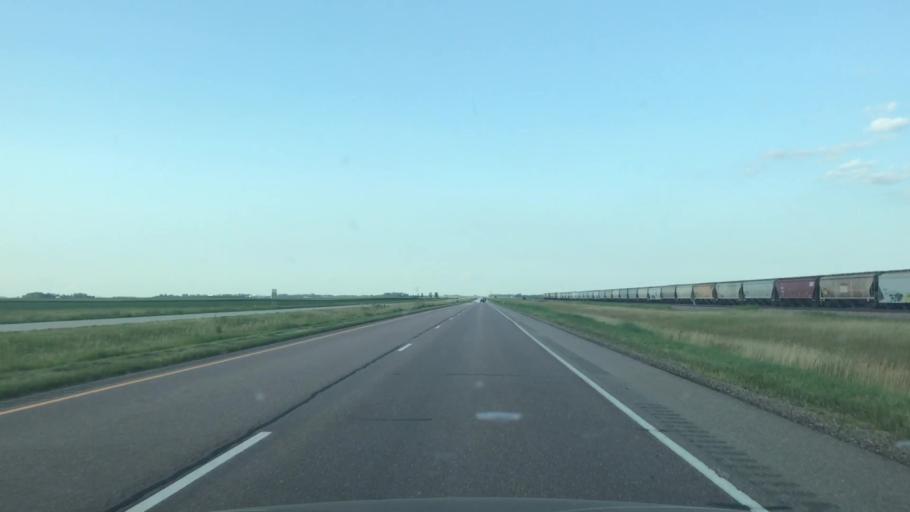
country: US
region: Minnesota
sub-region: Nobles County
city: Worthington
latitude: 43.7233
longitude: -95.4336
